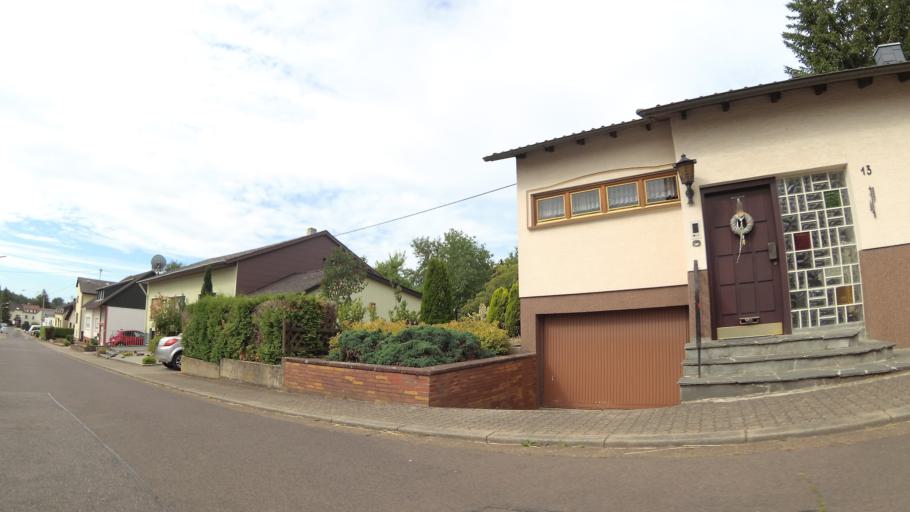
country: DE
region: Saarland
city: Schwalbach
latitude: 49.3237
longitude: 6.8209
